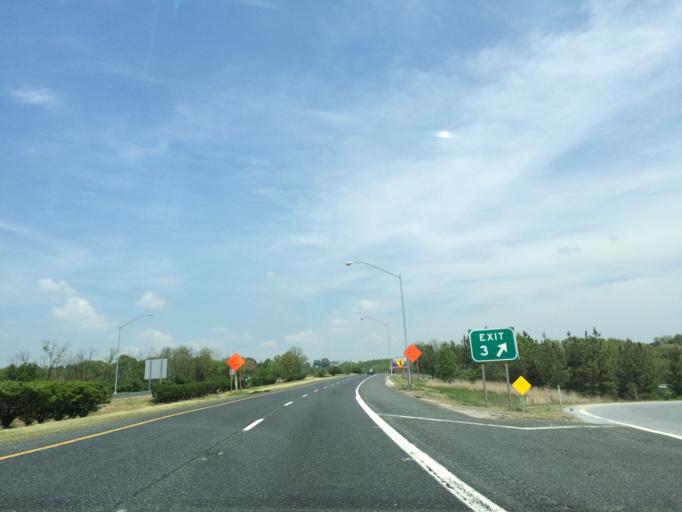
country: US
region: Maryland
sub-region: Howard County
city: Elkridge
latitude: 39.2224
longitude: -76.7020
